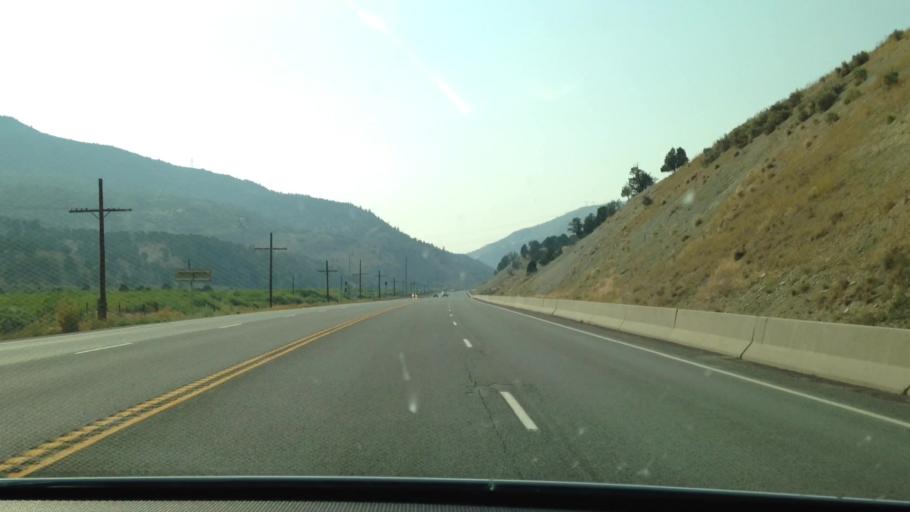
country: US
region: Utah
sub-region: Utah County
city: Mapleton
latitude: 39.9762
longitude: -111.3435
